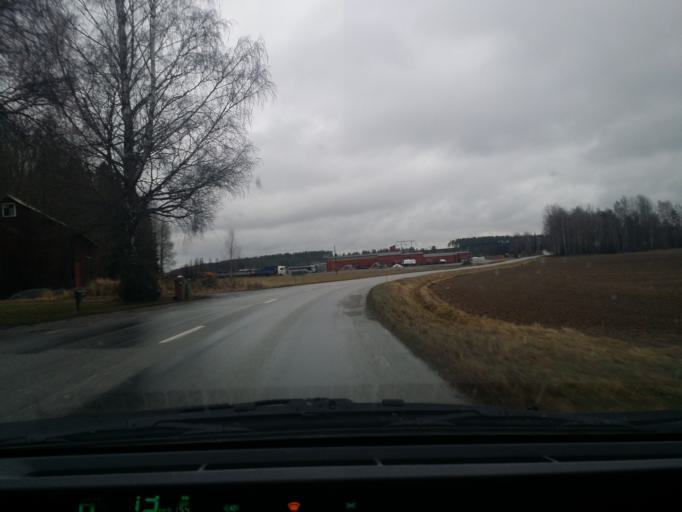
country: SE
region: Vaestmanland
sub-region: Vasteras
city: Skultuna
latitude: 59.8056
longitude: 16.5250
